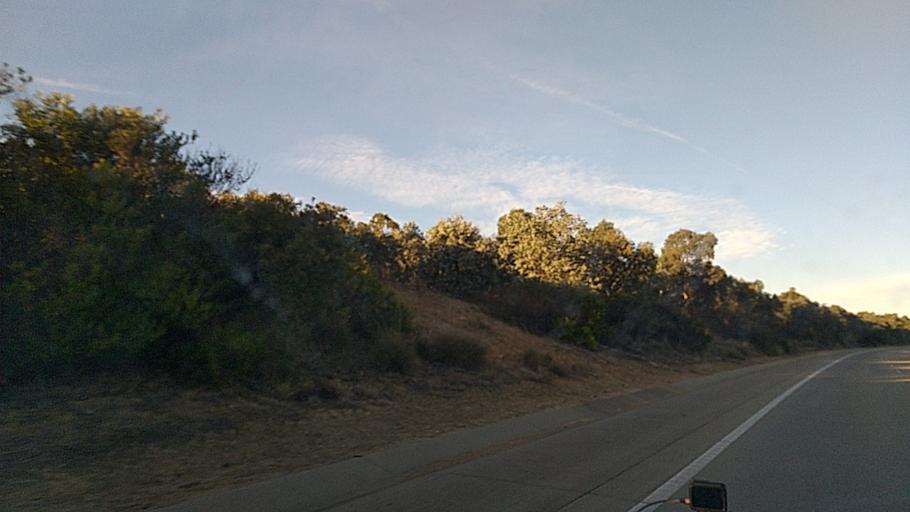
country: AU
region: New South Wales
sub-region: Yass Valley
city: Gundaroo
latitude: -35.1080
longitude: 149.3705
